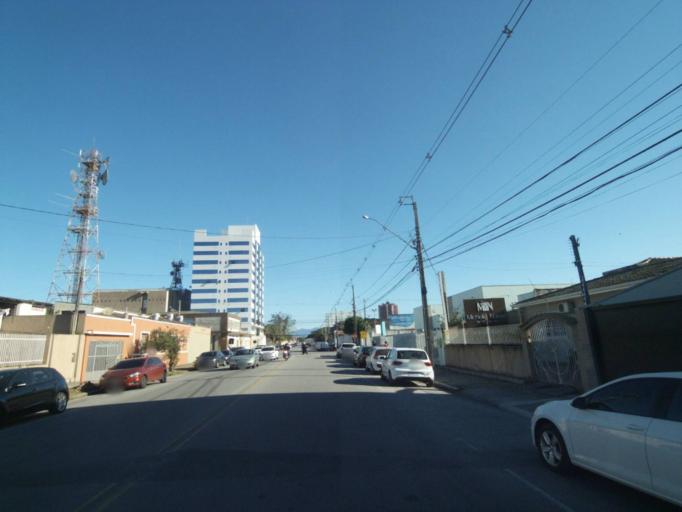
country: BR
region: Parana
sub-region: Paranagua
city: Paranagua
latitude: -25.5147
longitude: -48.5118
